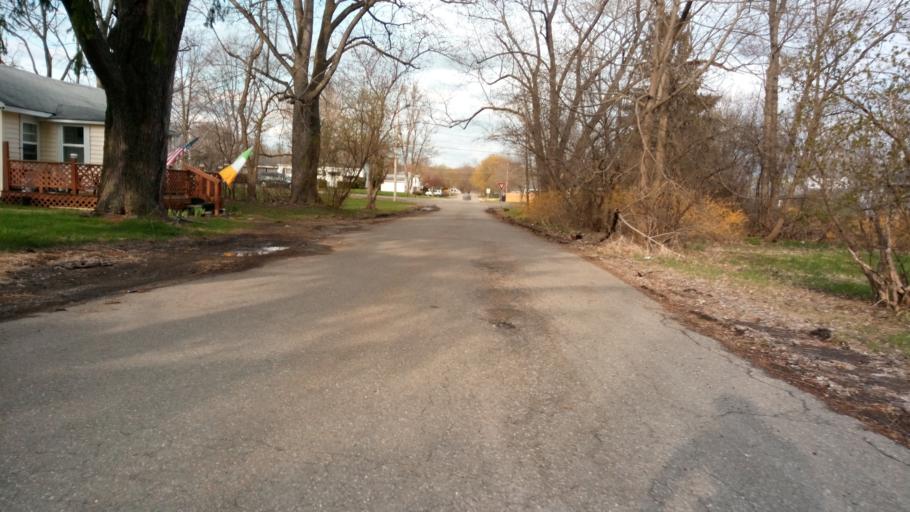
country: US
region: New York
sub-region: Chemung County
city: Southport
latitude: 42.0714
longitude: -76.8244
